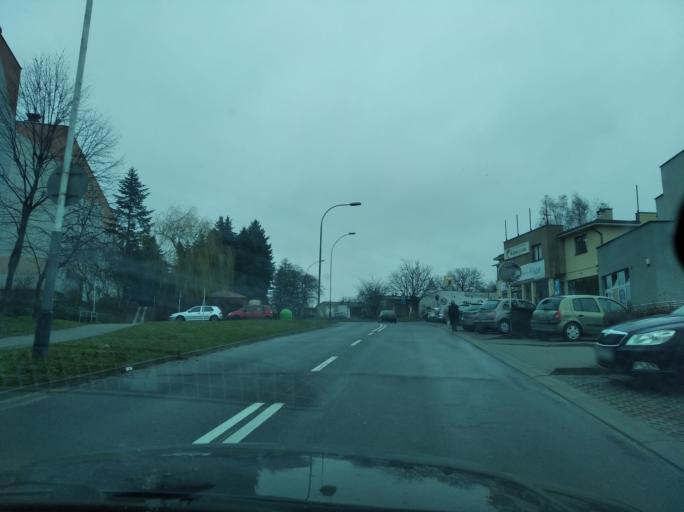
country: PL
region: Subcarpathian Voivodeship
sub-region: Rzeszow
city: Rzeszow
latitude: 50.0576
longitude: 21.9867
